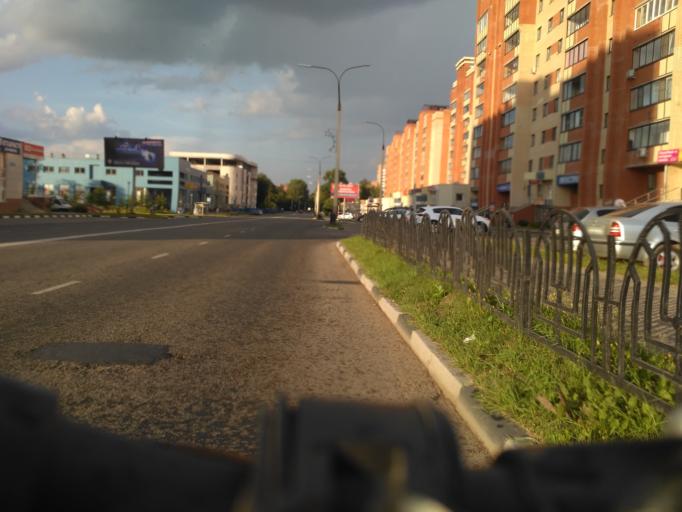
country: RU
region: Moskovskaya
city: Dubna
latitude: 56.7289
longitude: 37.1415
